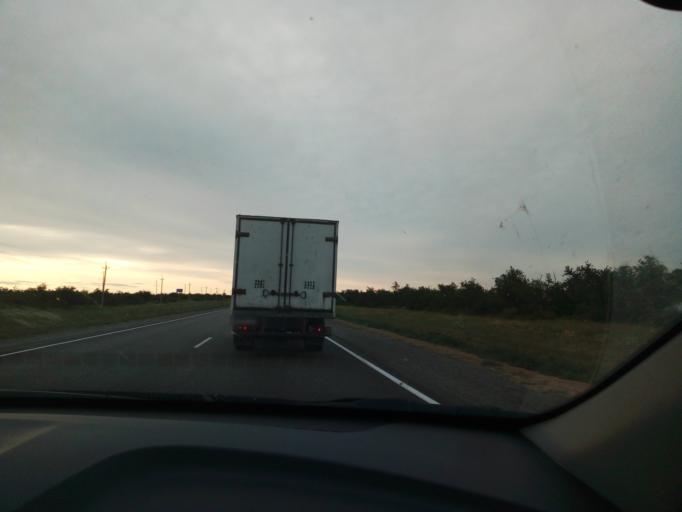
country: RU
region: Volgograd
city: Primorsk
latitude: 49.2280
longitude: 44.9026
